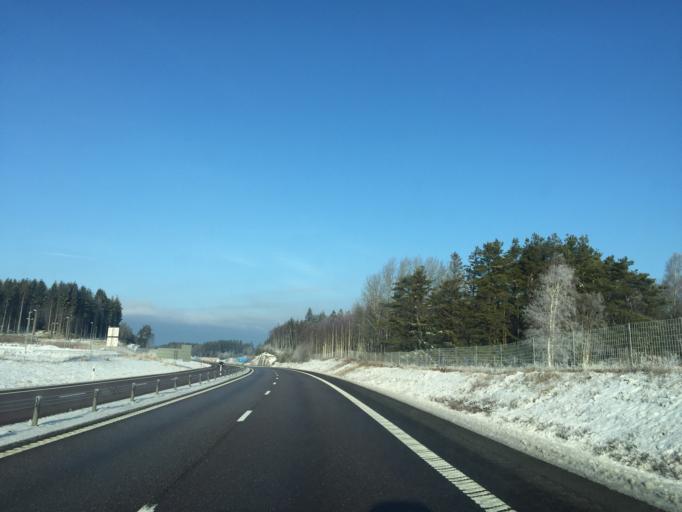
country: SE
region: Vaestra Goetaland
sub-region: Tanums Kommun
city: Tanumshede
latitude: 58.7236
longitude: 11.3508
